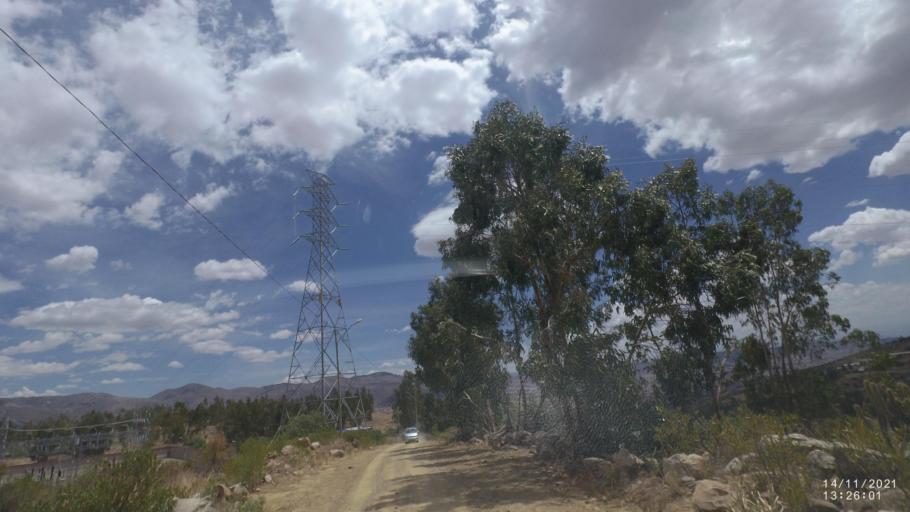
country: BO
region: Cochabamba
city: Colomi
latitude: -17.3832
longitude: -65.9811
